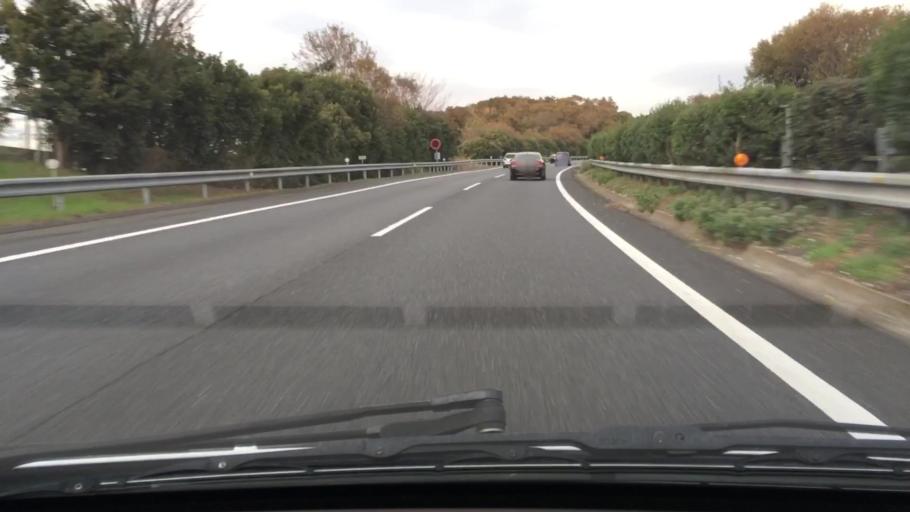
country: JP
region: Chiba
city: Kisarazu
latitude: 35.4215
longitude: 140.0142
